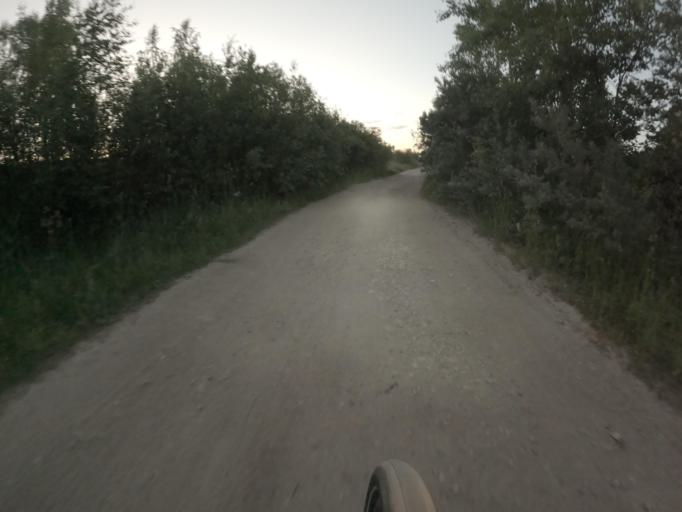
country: RU
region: St.-Petersburg
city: Sapernyy
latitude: 59.7816
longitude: 30.6735
